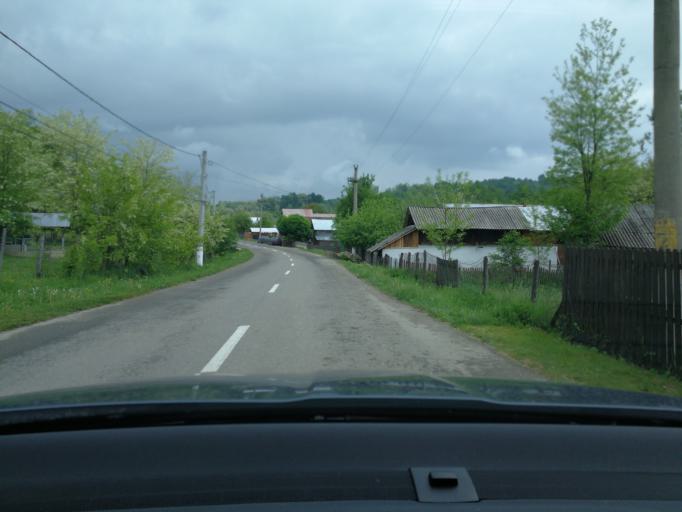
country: RO
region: Prahova
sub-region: Comuna Alunis
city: Alunis
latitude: 45.2049
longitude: 25.8471
